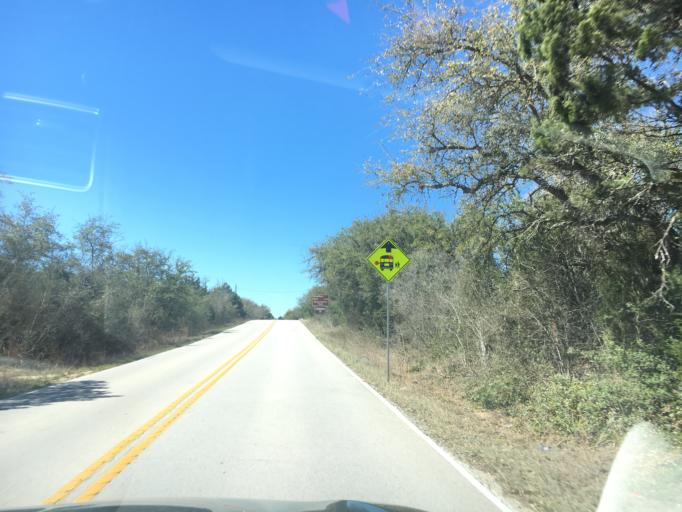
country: US
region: Texas
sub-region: Hays County
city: Dripping Springs
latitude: 30.2885
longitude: -98.0689
